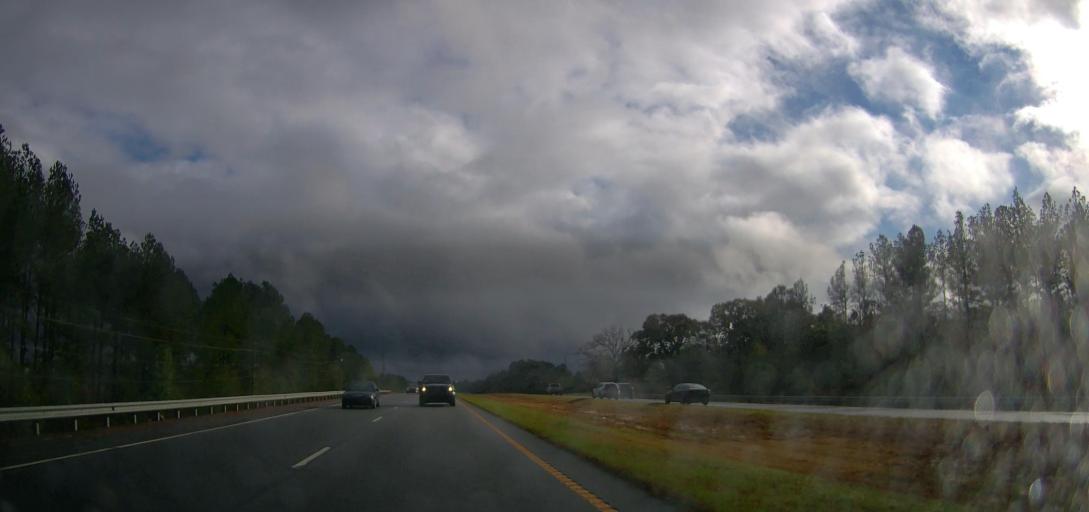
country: US
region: Georgia
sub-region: Clarke County
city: Country Club Estates
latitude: 34.0465
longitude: -83.4051
